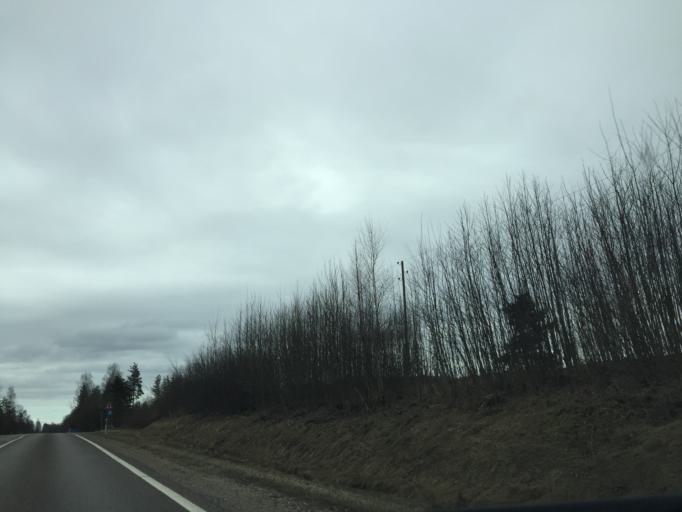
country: LV
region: Kraslavas Rajons
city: Kraslava
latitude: 55.9051
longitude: 27.1064
